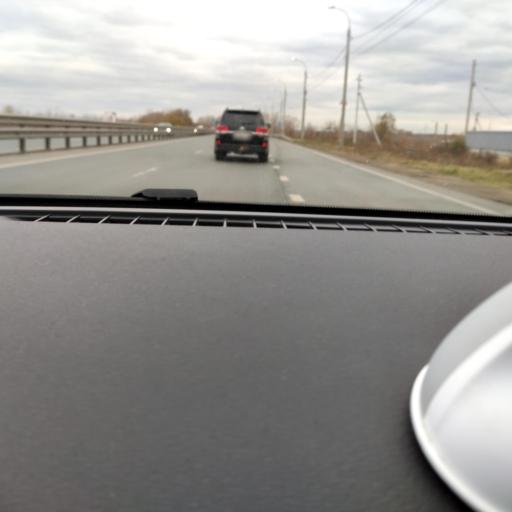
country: RU
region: Samara
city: Samara
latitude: 53.0980
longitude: 50.1589
